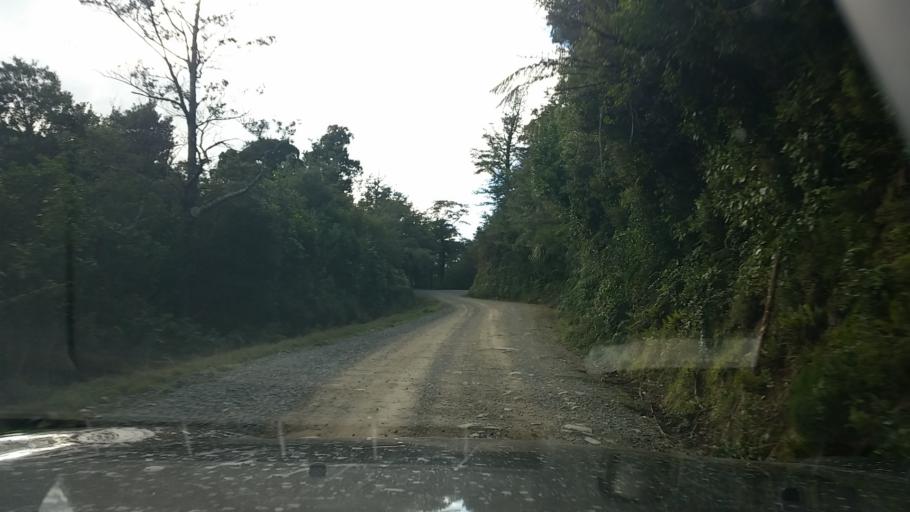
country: NZ
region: Marlborough
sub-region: Marlborough District
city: Picton
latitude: -41.1122
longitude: 174.1320
